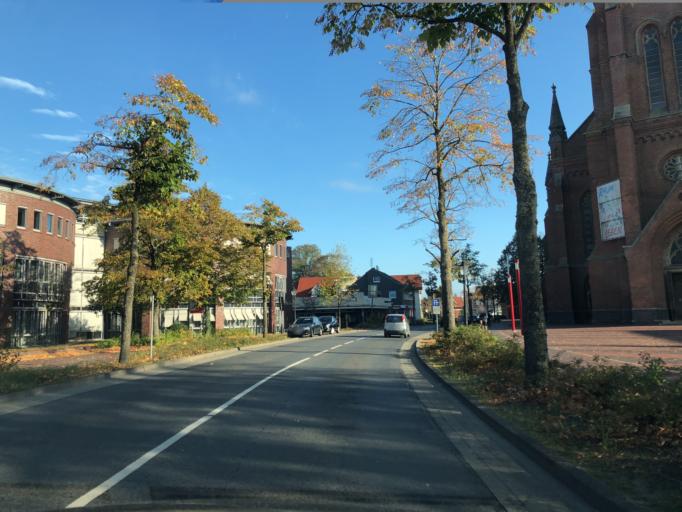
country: DE
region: Lower Saxony
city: Papenburg
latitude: 53.0788
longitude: 7.3938
